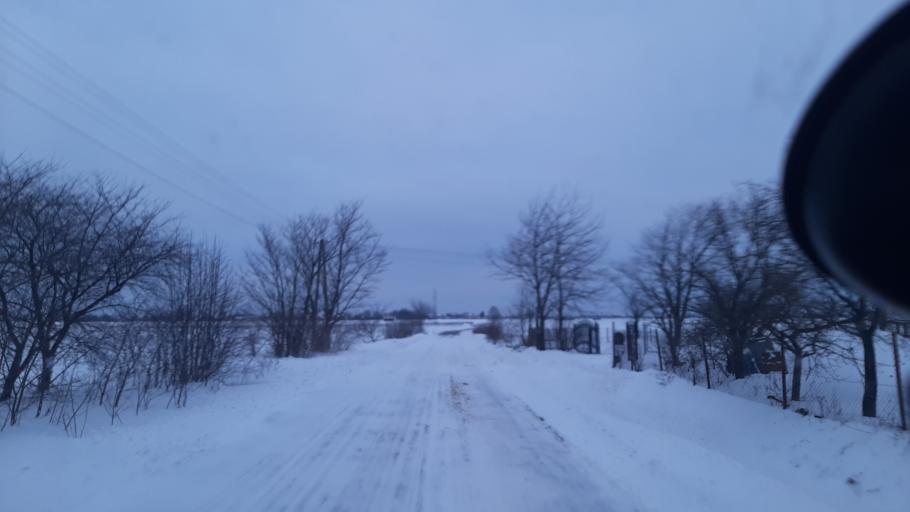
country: PL
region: Lublin Voivodeship
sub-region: Powiat lubelski
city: Jastkow
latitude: 51.3464
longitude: 22.4092
